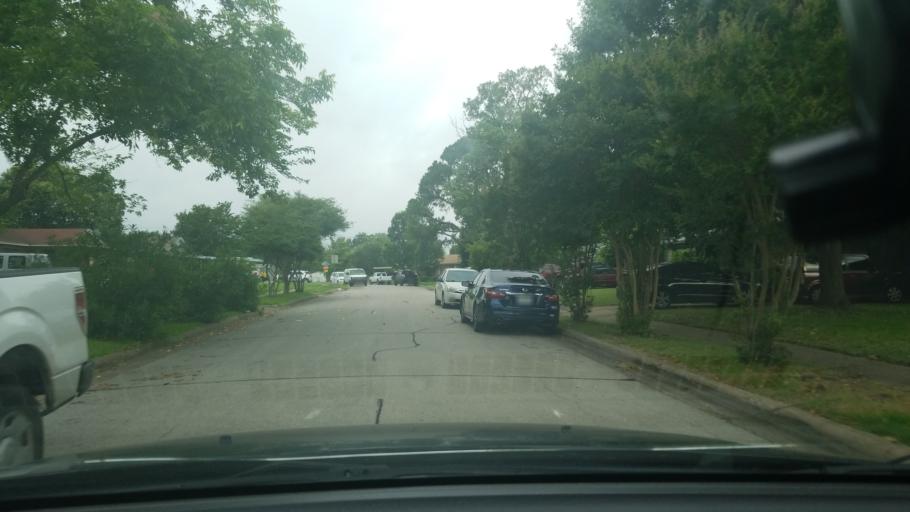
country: US
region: Texas
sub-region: Dallas County
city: Mesquite
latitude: 32.7882
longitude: -96.6303
